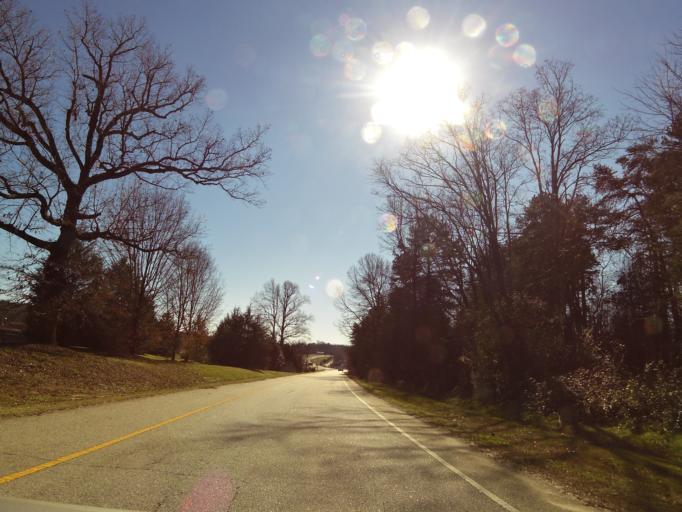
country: US
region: South Carolina
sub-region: Greenville County
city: Travelers Rest
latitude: 34.9568
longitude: -82.4397
